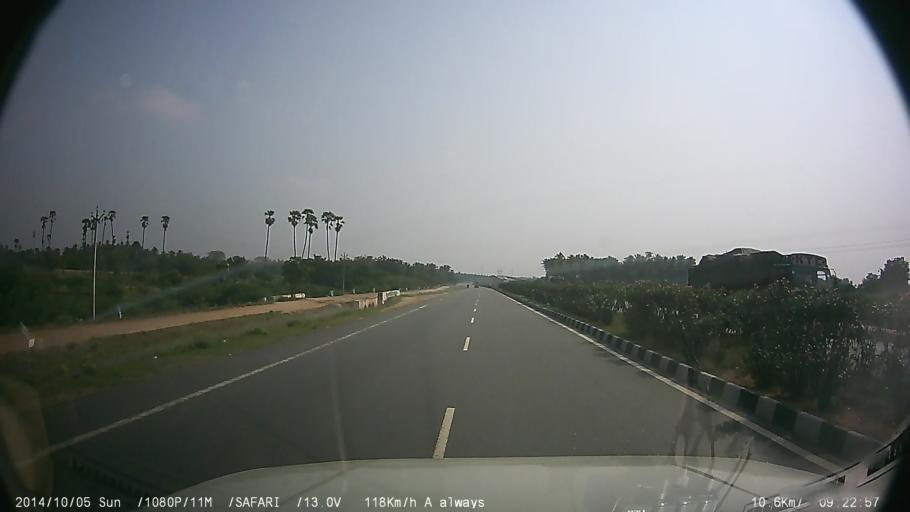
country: IN
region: Tamil Nadu
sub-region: Erode
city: Perundurai
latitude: 11.2951
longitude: 77.5932
